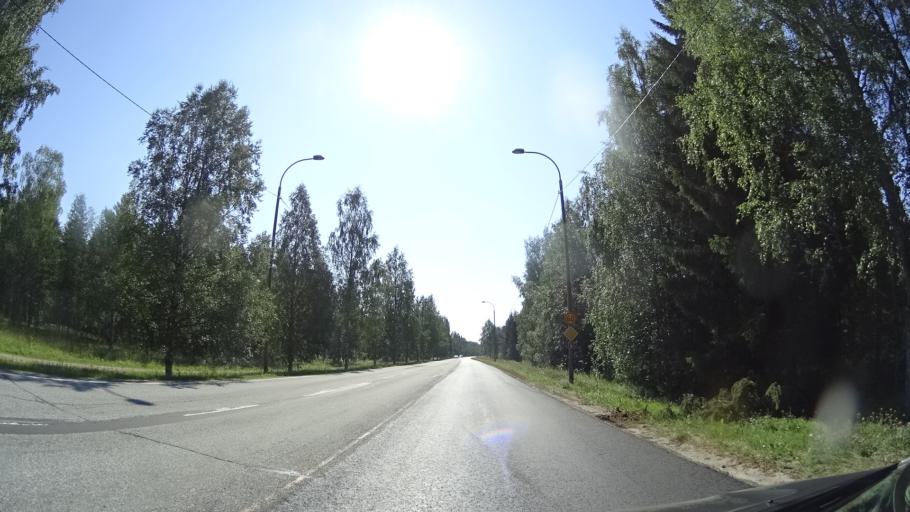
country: FI
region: North Karelia
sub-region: Joensuu
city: Juuka
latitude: 63.2465
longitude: 29.2686
